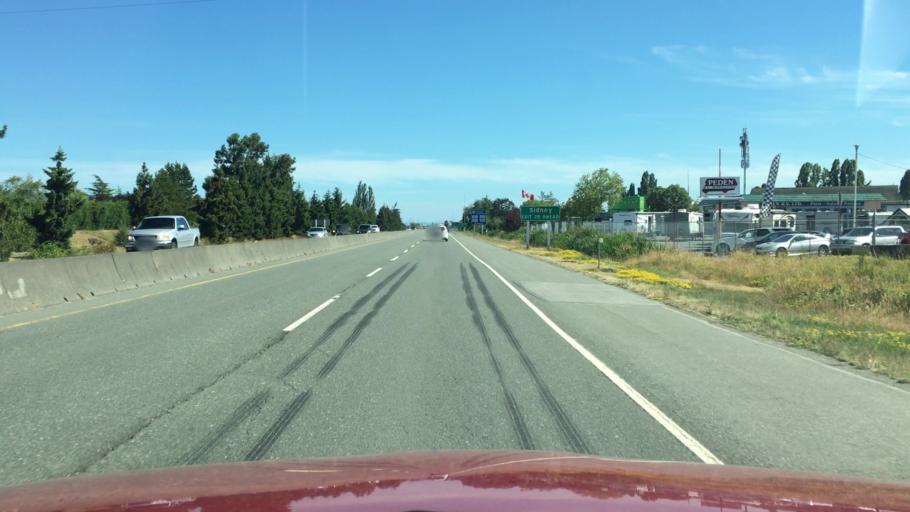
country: CA
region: British Columbia
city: North Saanich
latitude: 48.6556
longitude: -123.4120
